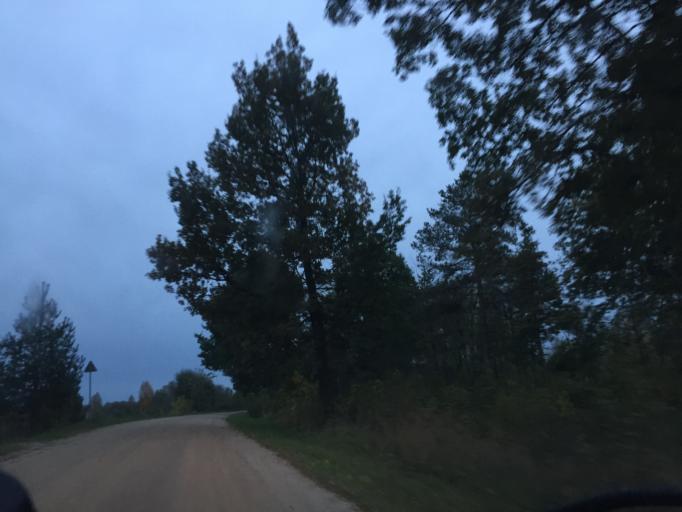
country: LV
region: Adazi
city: Adazi
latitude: 57.0809
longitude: 24.3688
